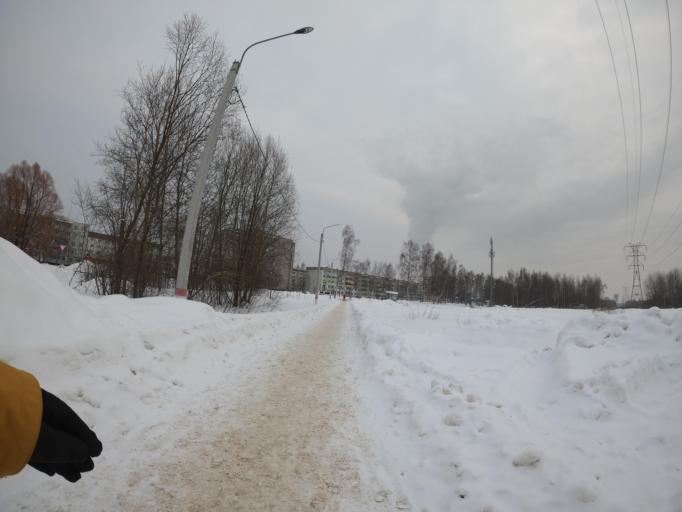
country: RU
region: Moskovskaya
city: Elektrogorsk
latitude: 55.8707
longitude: 38.7800
